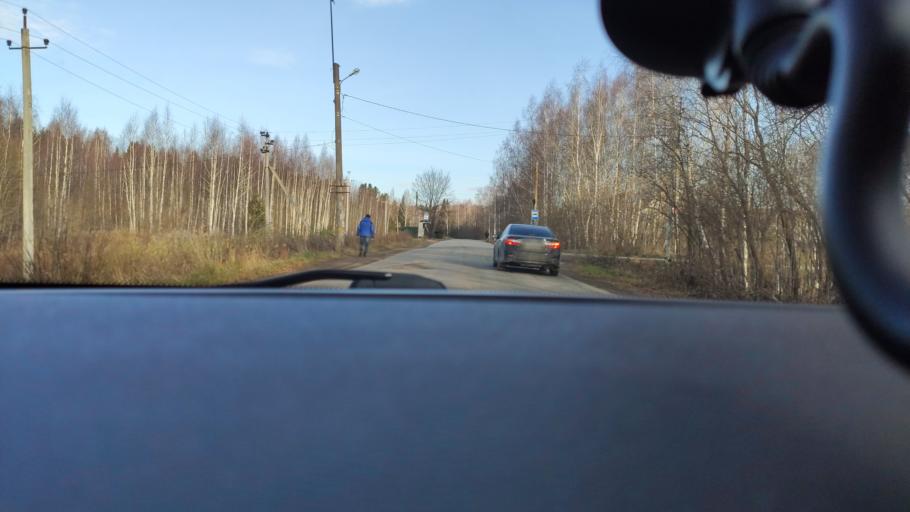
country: RU
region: Perm
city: Kondratovo
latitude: 58.0577
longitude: 56.0275
